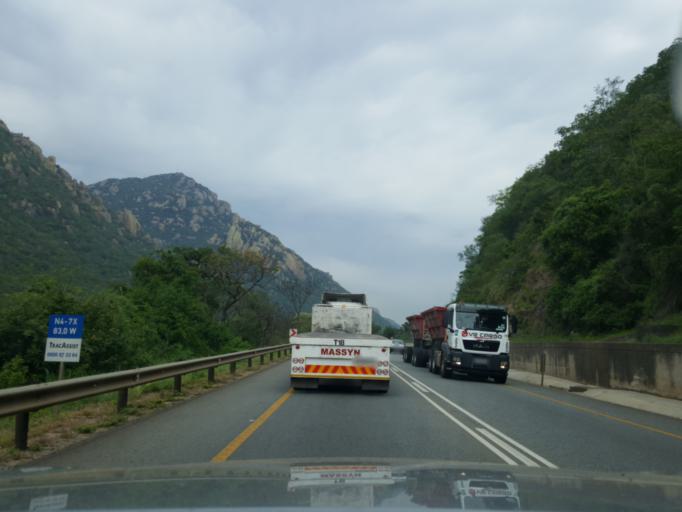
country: ZA
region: Mpumalanga
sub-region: Ehlanzeni District
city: Nelspruit
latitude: -25.5202
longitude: 31.2467
